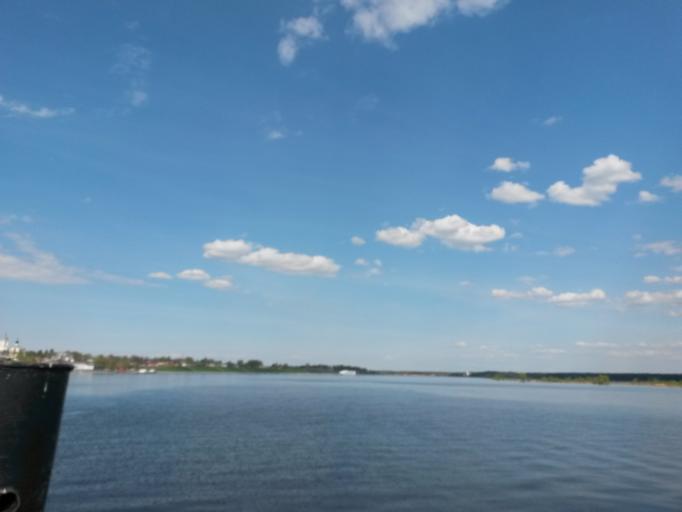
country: RU
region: Jaroslavl
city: Myshkin
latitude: 57.7778
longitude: 38.4544
